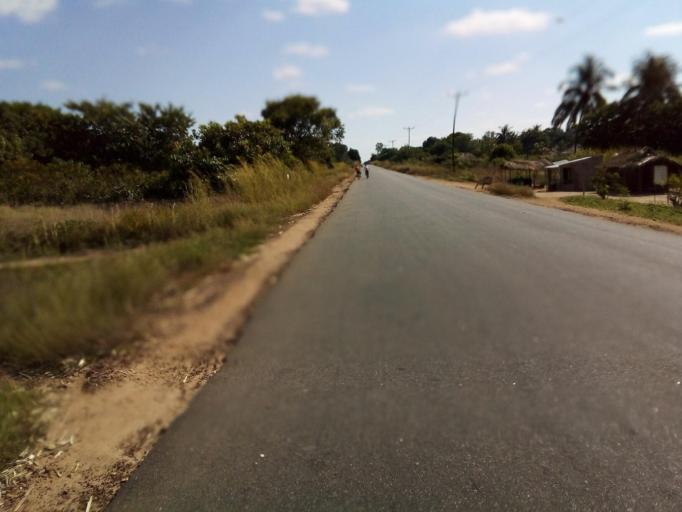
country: MZ
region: Zambezia
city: Quelimane
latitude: -17.5774
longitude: 36.6669
